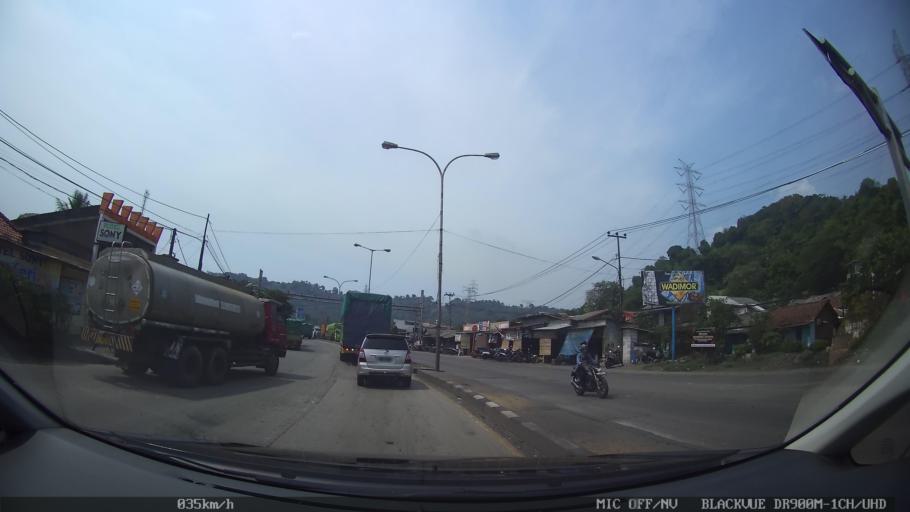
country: ID
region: Banten
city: Kubangkepuh
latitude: -5.9379
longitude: 106.0020
